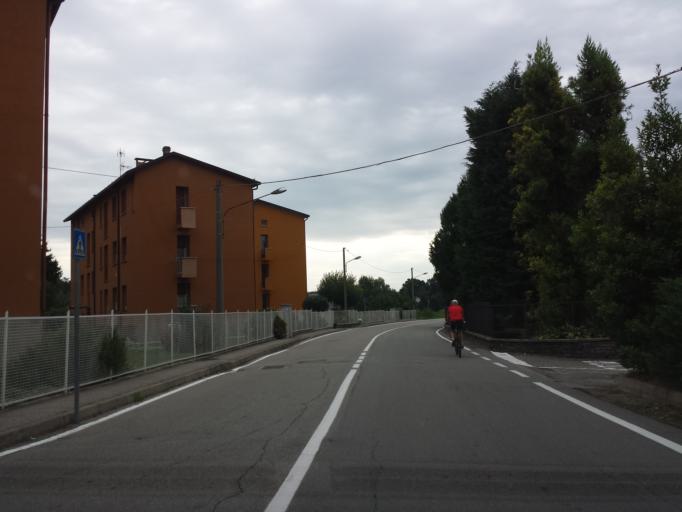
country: IT
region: Lombardy
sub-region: Provincia di Varese
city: Sesto Calende
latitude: 45.7326
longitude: 8.6236
